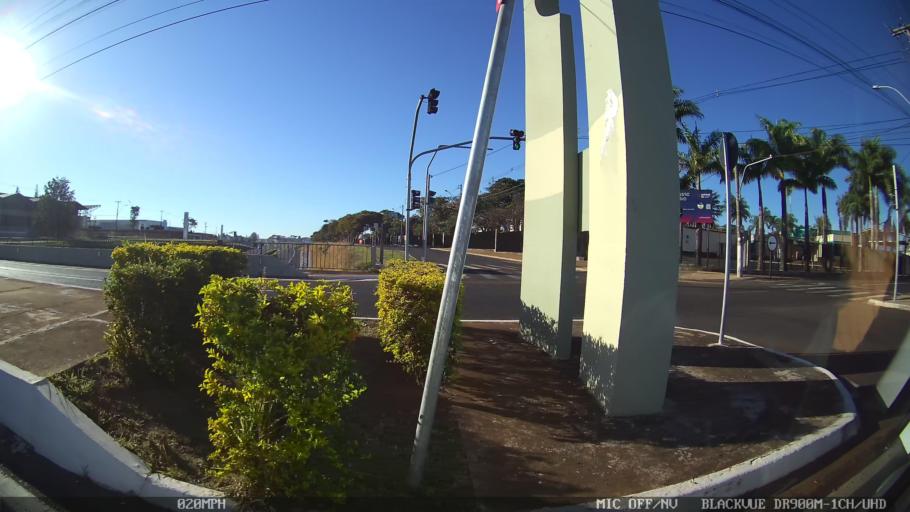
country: BR
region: Sao Paulo
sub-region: Franca
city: Franca
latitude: -20.5685
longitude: -47.4052
